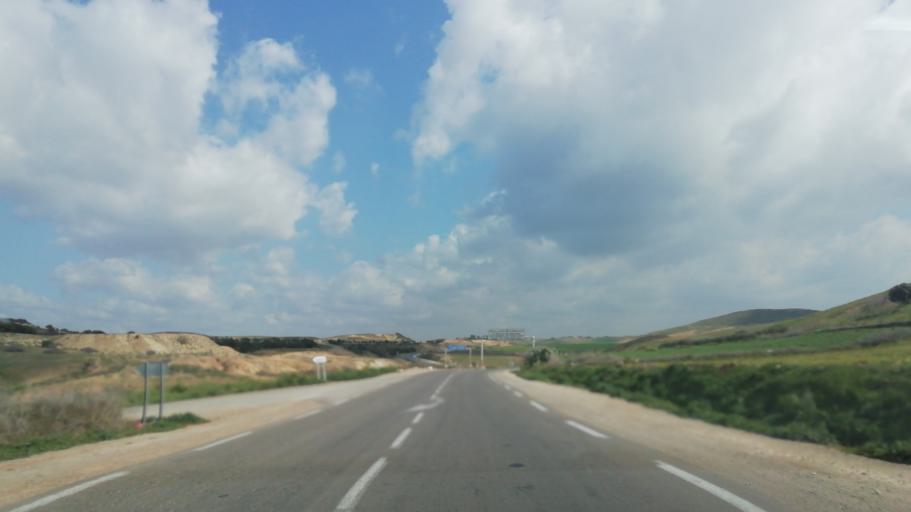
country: DZ
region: Mostaganem
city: Mostaganem
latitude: 35.7020
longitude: 0.2323
